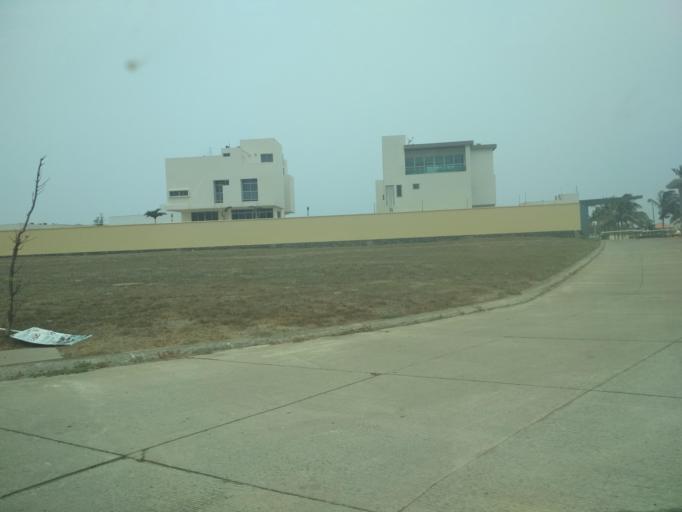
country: MX
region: Veracruz
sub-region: Alvarado
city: Playa de la Libertad
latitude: 19.0628
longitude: -96.0750
